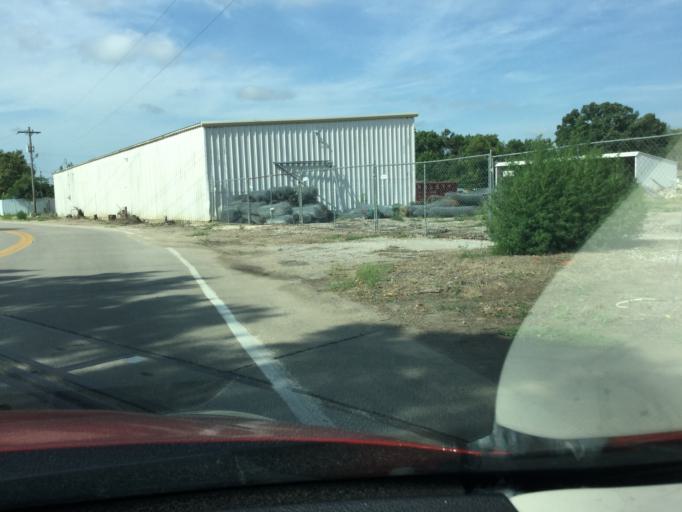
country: US
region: Kansas
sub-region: Shawnee County
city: Topeka
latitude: 39.0704
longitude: -95.6731
